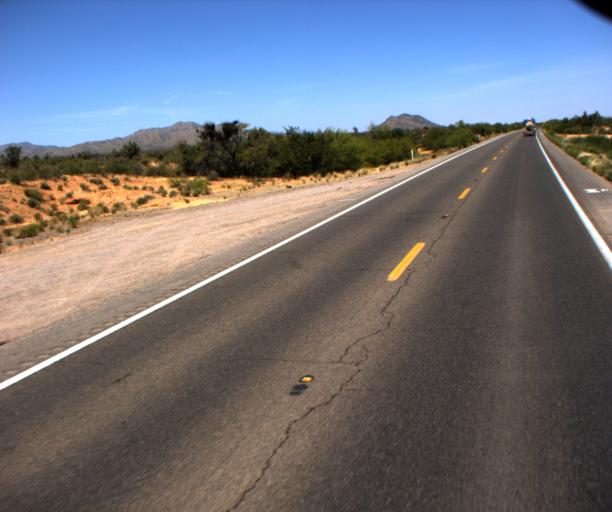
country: US
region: Arizona
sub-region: Gila County
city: Peridot
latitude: 33.3098
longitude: -110.5023
